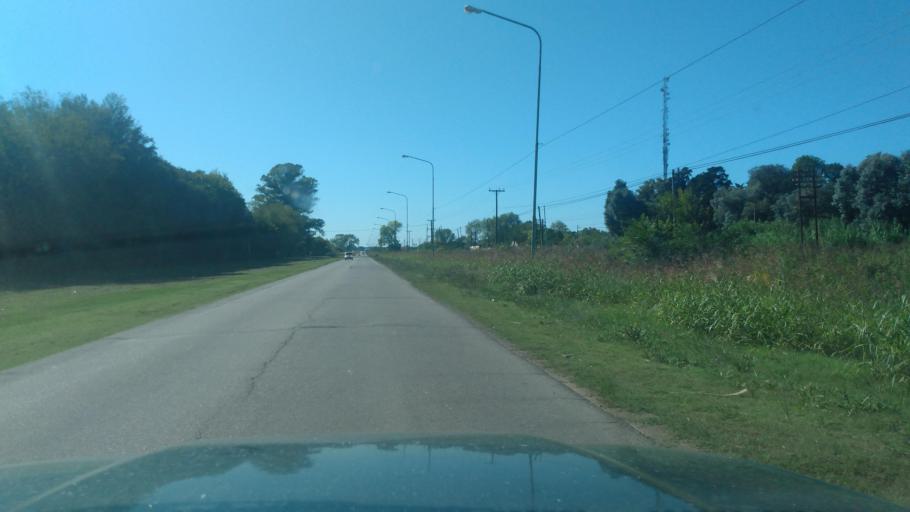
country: AR
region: Buenos Aires
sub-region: Partido de Lujan
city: Lujan
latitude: -34.5850
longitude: -59.0537
